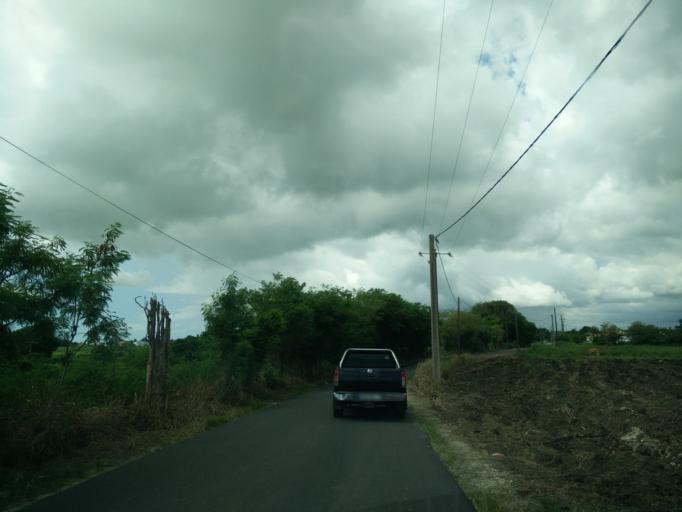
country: GP
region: Guadeloupe
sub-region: Guadeloupe
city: Le Moule
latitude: 16.2987
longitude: -61.3431
